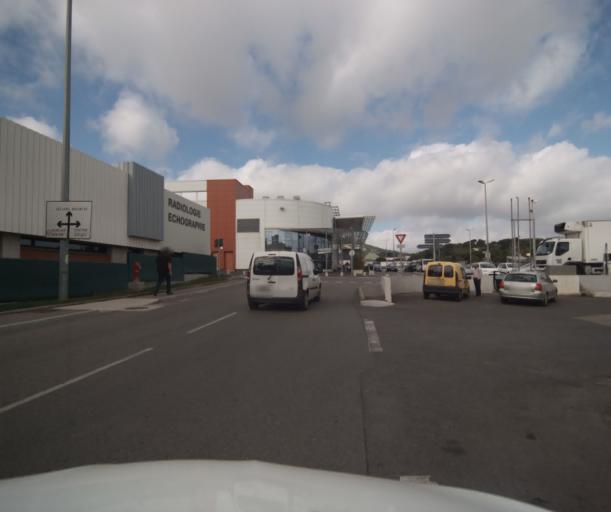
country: FR
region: Provence-Alpes-Cote d'Azur
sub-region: Departement du Var
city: Six-Fours-les-Plages
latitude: 43.1095
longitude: 5.8603
